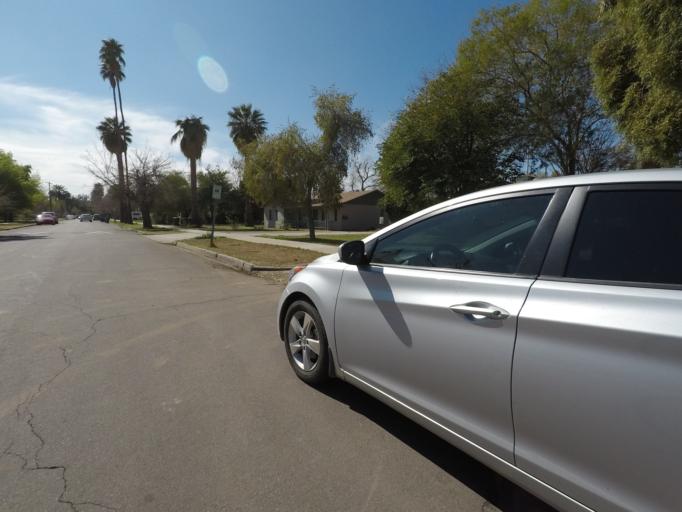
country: US
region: Arizona
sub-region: Maricopa County
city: Tempe Junction
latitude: 33.4186
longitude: -111.9425
